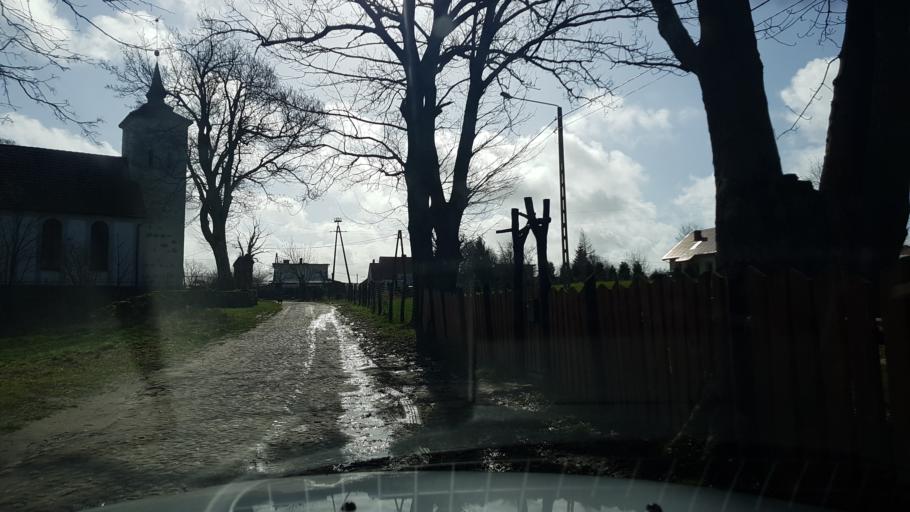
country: PL
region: Pomeranian Voivodeship
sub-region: Powiat slupski
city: Ustka
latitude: 54.5226
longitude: 16.7656
